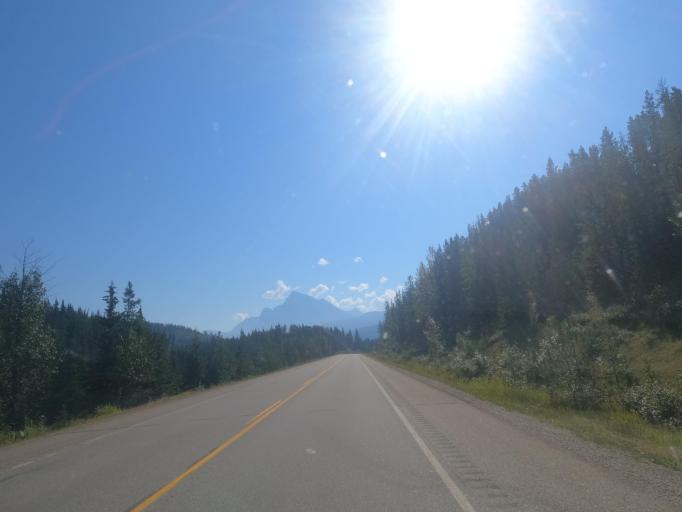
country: CA
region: Alberta
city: Jasper Park Lodge
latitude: 52.8577
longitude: -118.6305
